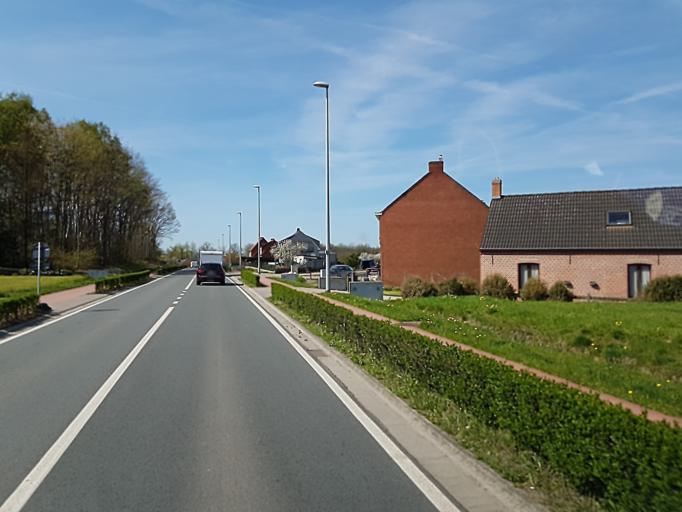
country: BE
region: Flanders
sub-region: Provincie Antwerpen
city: Westerlo
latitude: 51.0717
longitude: 4.8981
